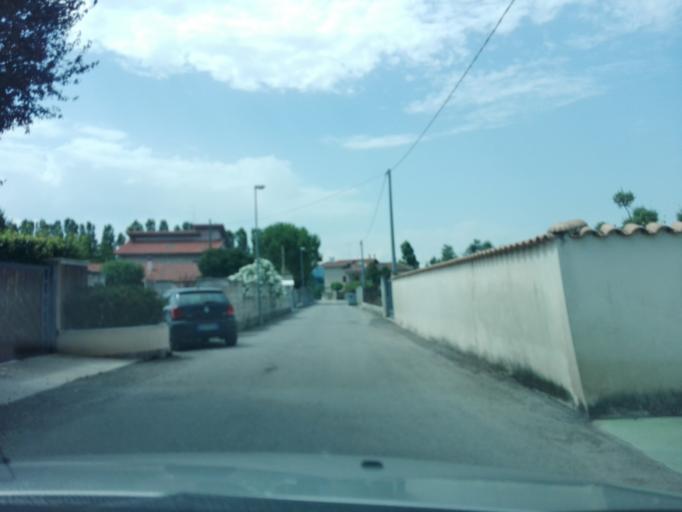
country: IT
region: Abruzzo
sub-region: Provincia di Pescara
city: Cappelle sul Tavo
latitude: 42.4902
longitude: 14.1194
